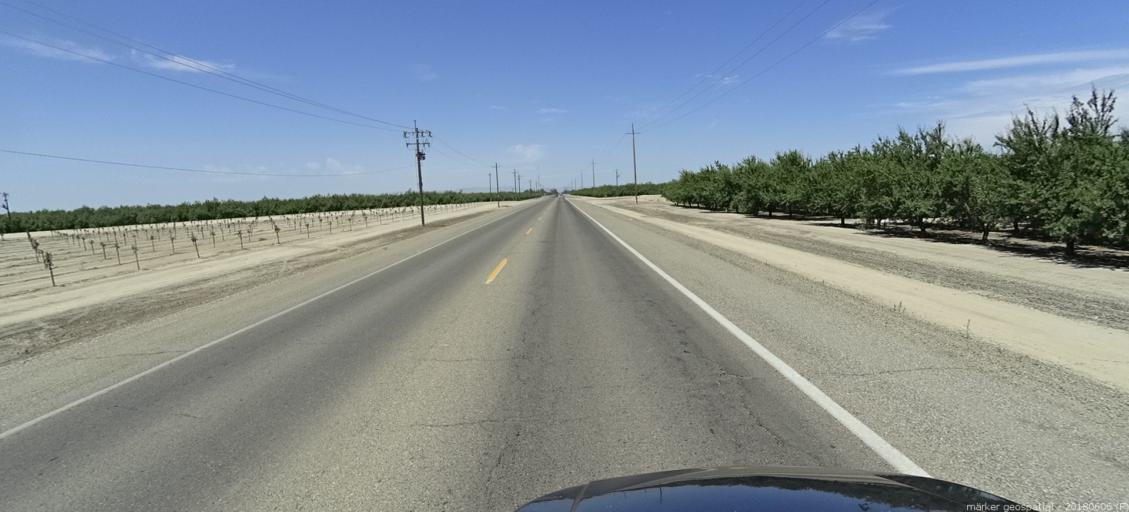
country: US
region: California
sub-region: Fresno County
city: Firebaugh
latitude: 36.8586
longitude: -120.3836
